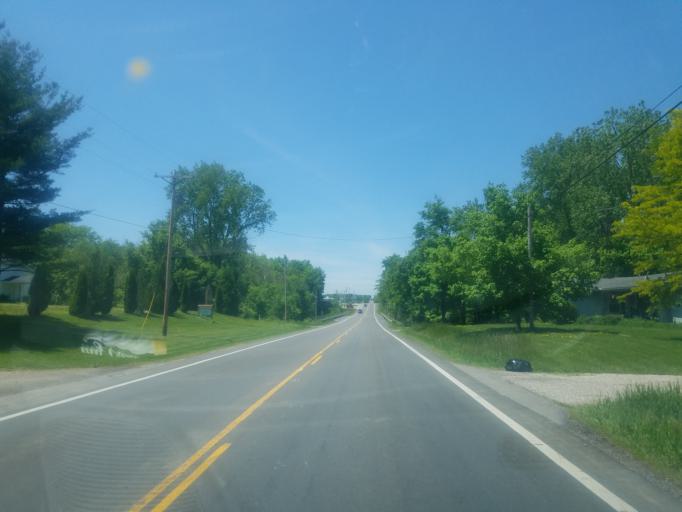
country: US
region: Ohio
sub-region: Huron County
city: New London
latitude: 41.0294
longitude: -82.4131
